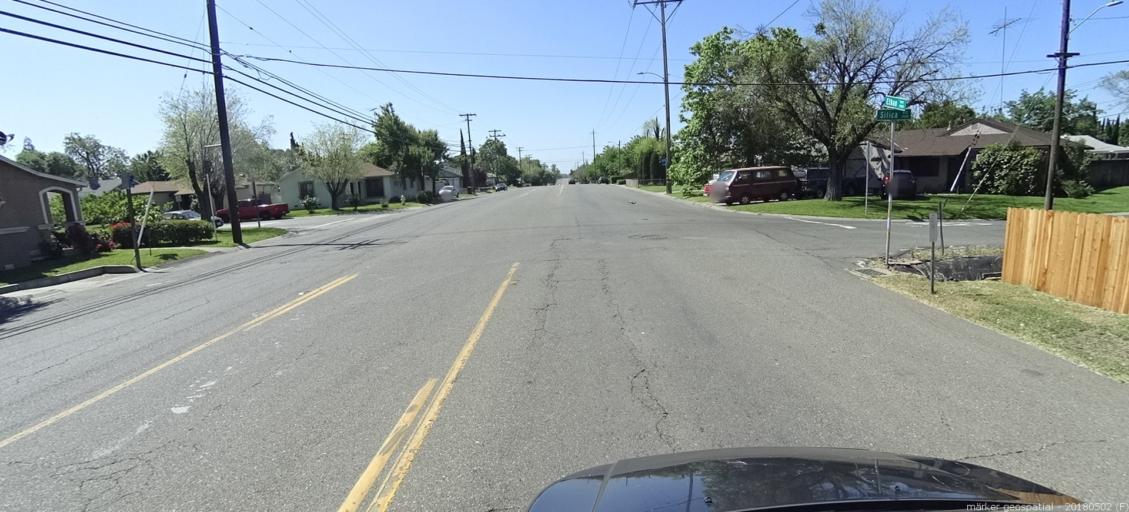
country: US
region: California
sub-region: Sacramento County
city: Arden-Arcade
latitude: 38.6088
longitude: -121.4200
